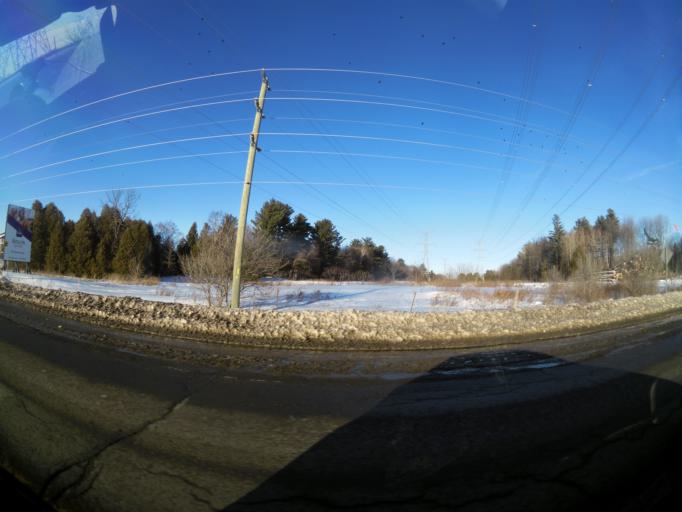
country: CA
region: Ontario
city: Ottawa
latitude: 45.4324
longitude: -75.5254
